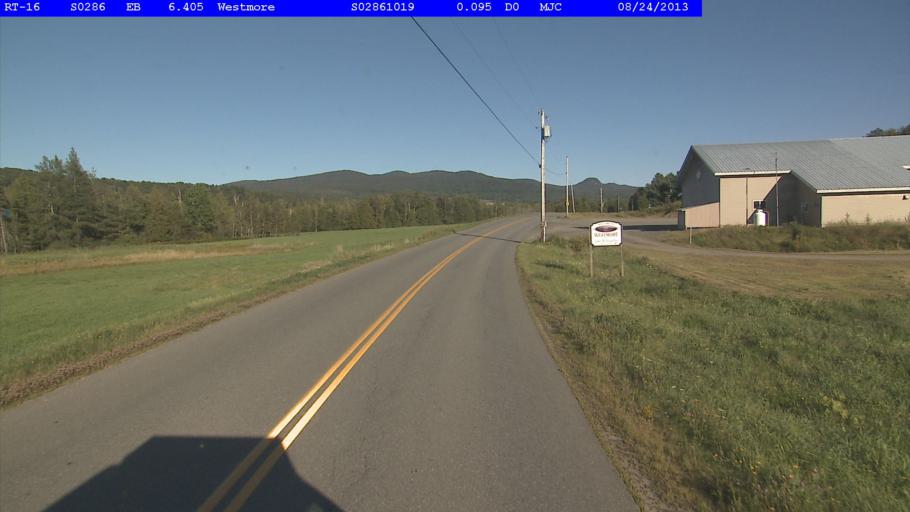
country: US
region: Vermont
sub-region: Orleans County
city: Newport
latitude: 44.7811
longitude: -72.0808
